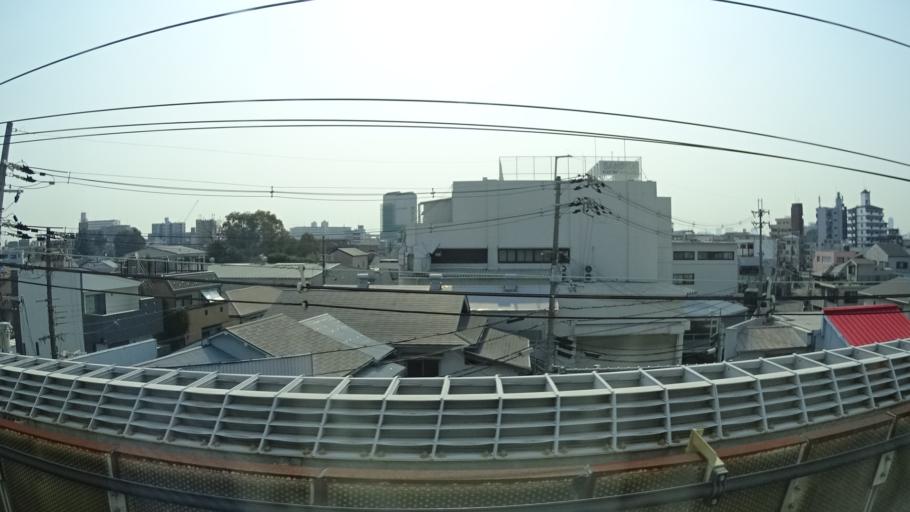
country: JP
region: Osaka
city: Suita
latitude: 34.7385
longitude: 135.5100
